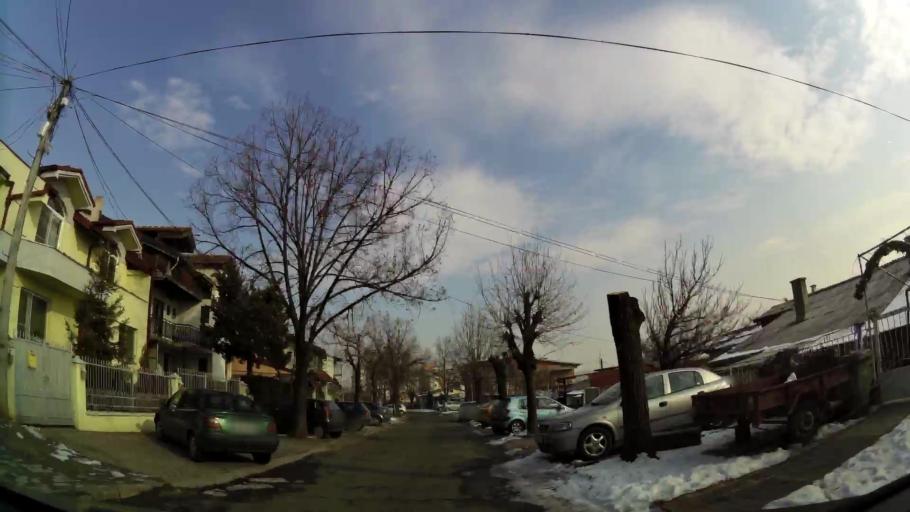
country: MK
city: Creshevo
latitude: 42.0054
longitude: 21.4987
